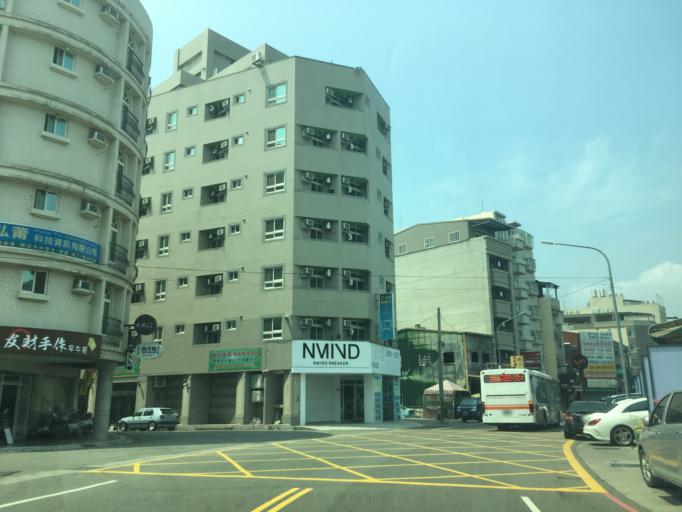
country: TW
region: Taiwan
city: Zhongxing New Village
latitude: 24.0432
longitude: 120.6890
